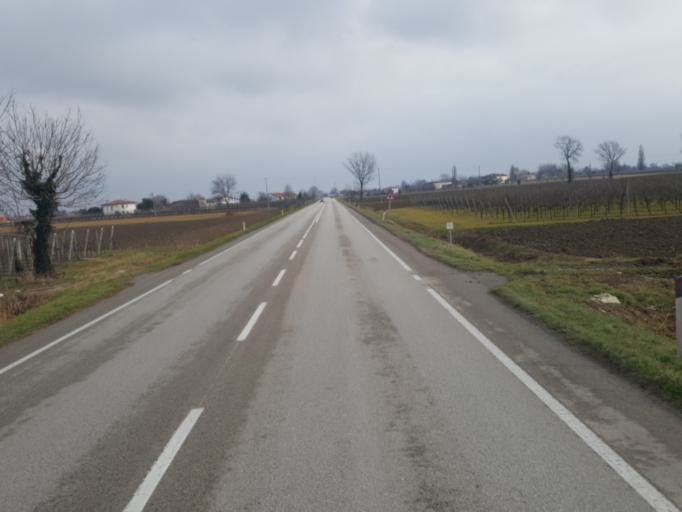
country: IT
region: Veneto
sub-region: Provincia di Padova
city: Pozzonovo
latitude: 45.2110
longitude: 11.7978
